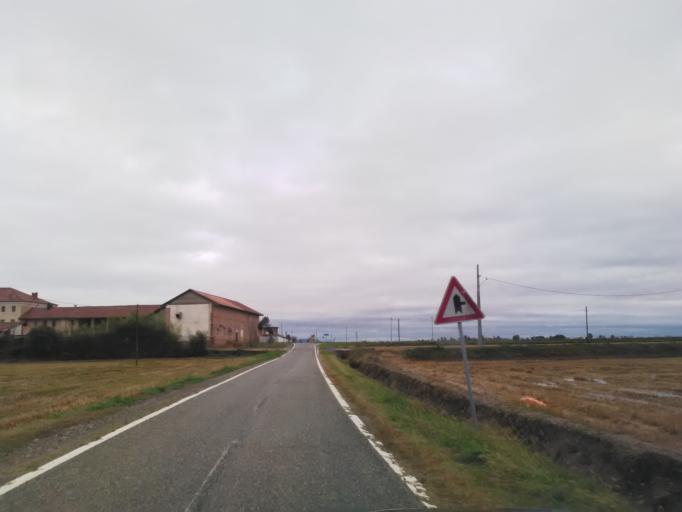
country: IT
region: Piedmont
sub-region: Provincia di Vercelli
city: Carisio
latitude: 45.4070
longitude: 8.2458
